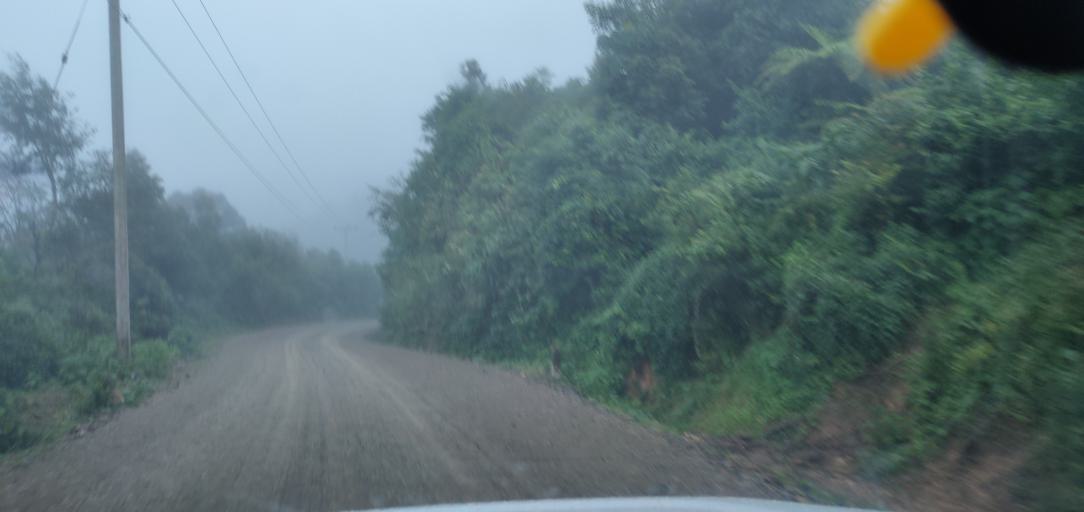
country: LA
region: Phongsali
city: Phongsali
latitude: 21.3913
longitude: 102.2016
